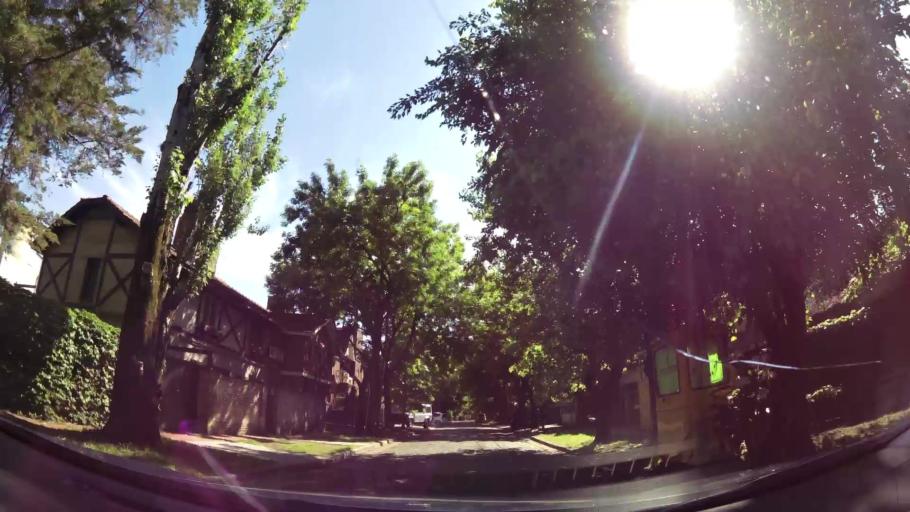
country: AR
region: Buenos Aires
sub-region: Partido de Tigre
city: Tigre
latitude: -34.4832
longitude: -58.5746
